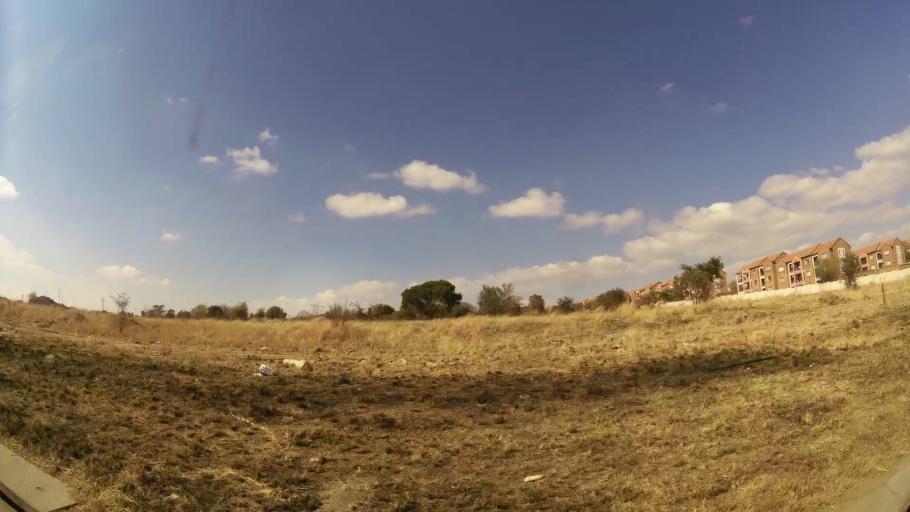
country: ZA
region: Gauteng
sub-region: City of Johannesburg Metropolitan Municipality
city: Midrand
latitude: -26.0074
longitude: 28.1088
